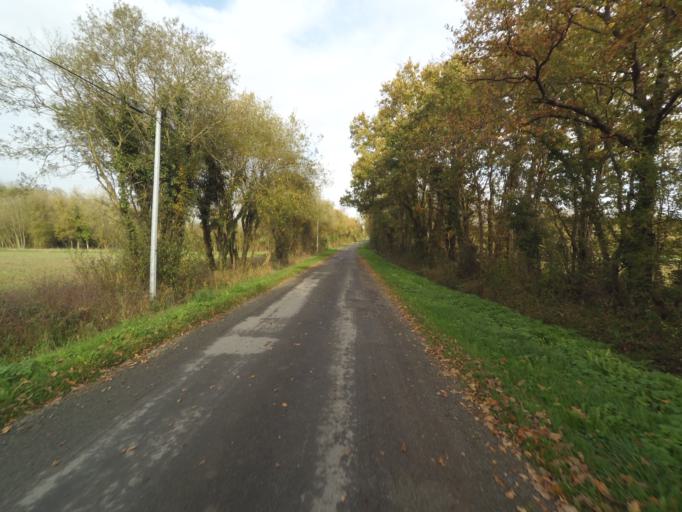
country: FR
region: Pays de la Loire
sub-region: Departement de la Vendee
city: Saint-Hilaire-de-Loulay
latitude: 47.0287
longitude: -1.3472
